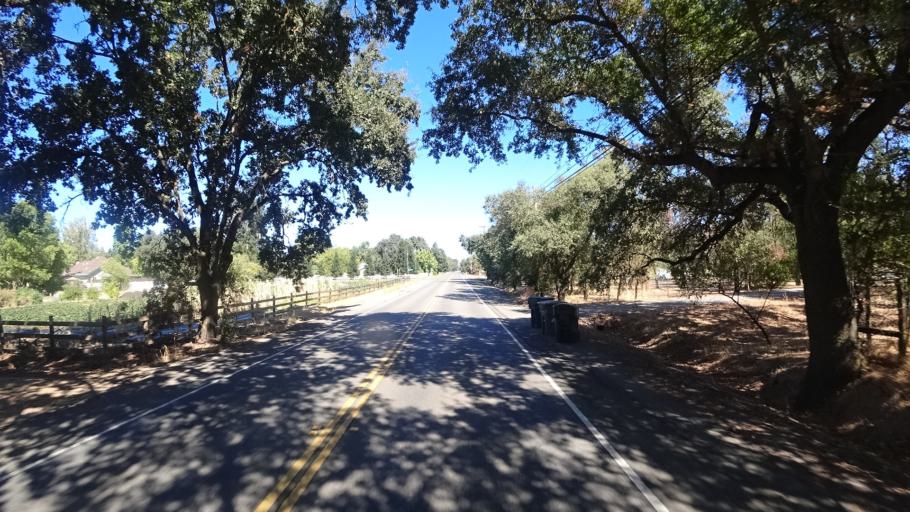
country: US
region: California
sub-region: Sacramento County
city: Vineyard
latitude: 38.4273
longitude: -121.3253
